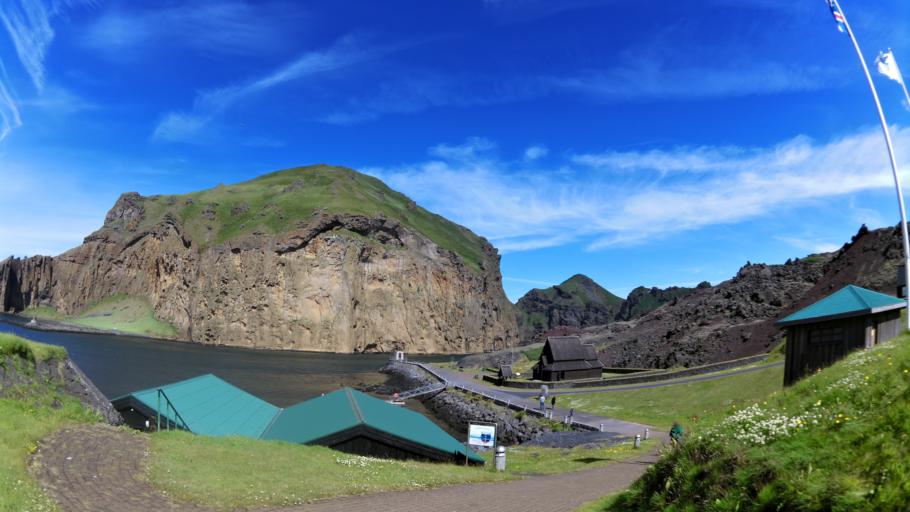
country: IS
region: South
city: Vestmannaeyjar
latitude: 63.4437
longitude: -20.2621
